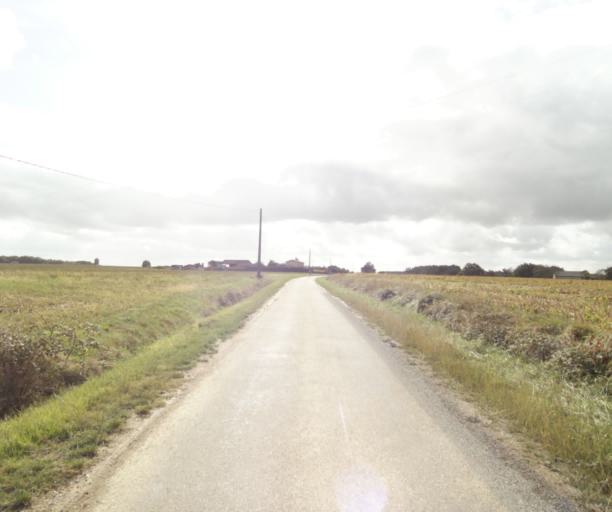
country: FR
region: Midi-Pyrenees
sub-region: Departement du Tarn-et-Garonne
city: Beaumont-de-Lomagne
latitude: 43.8705
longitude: 1.0687
